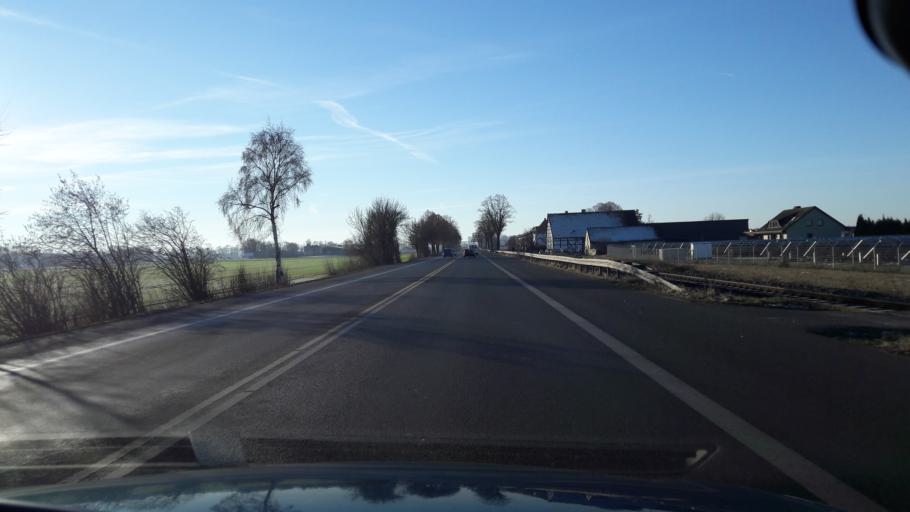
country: DE
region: North Rhine-Westphalia
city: Erwitte
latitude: 51.6407
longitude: 8.3423
